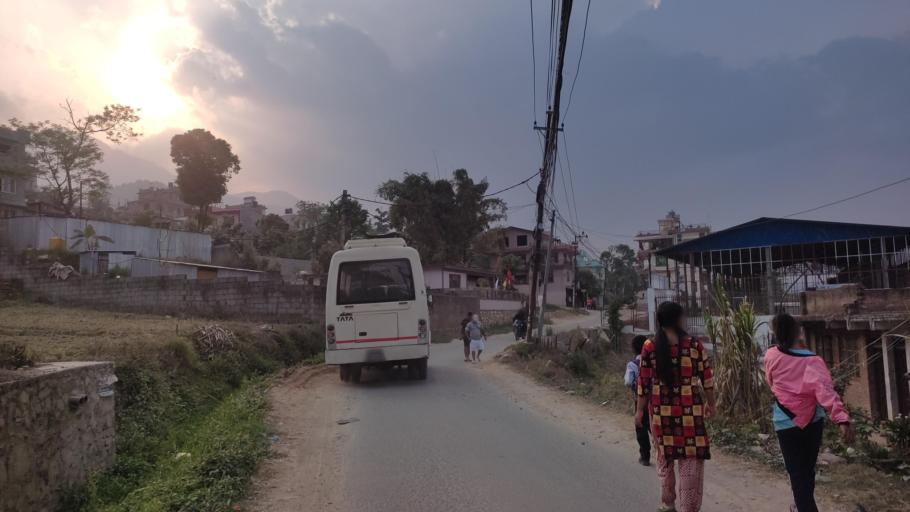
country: NP
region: Central Region
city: Kirtipur
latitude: 27.6713
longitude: 85.2481
